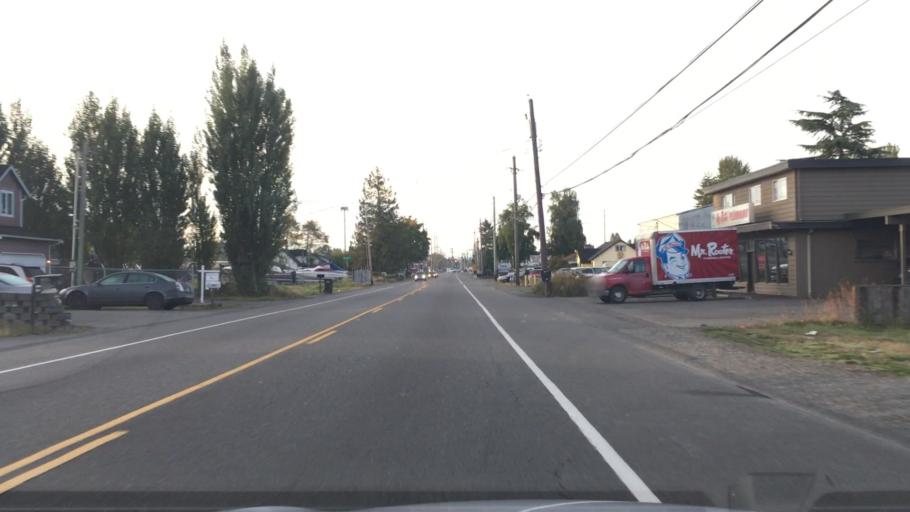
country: US
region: Washington
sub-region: Pierce County
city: Midland
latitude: 47.1716
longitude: -122.4054
